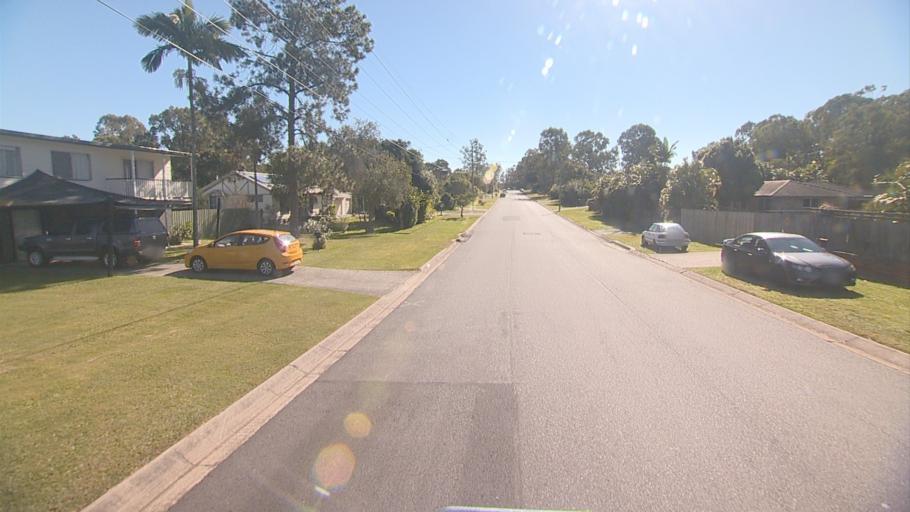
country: AU
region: Queensland
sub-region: Logan
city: Beenleigh
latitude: -27.6993
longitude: 153.2002
